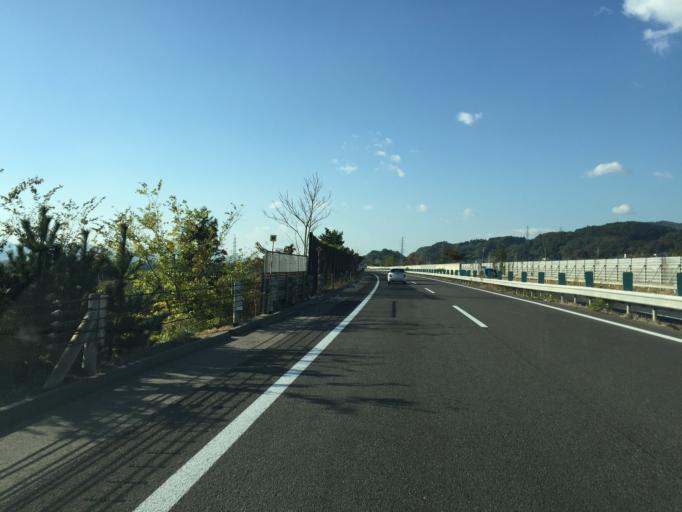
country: JP
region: Fukushima
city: Hobaramachi
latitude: 37.8751
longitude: 140.5248
